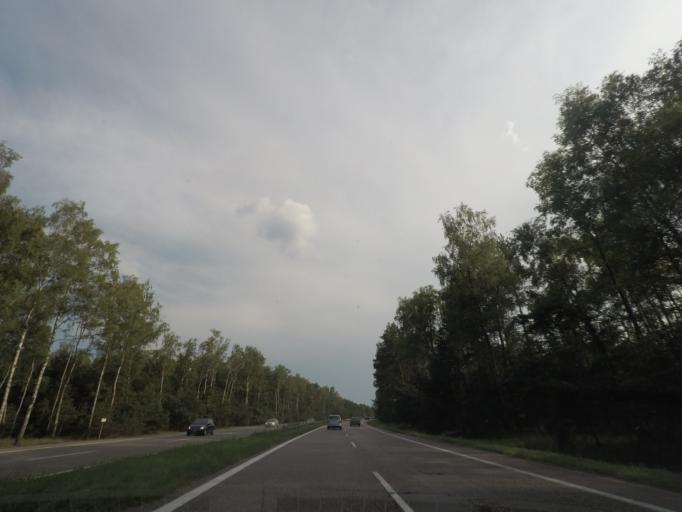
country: PL
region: Silesian Voivodeship
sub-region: Dabrowa Gornicza
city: Dabrowa Gornicza
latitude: 50.3673
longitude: 19.2503
